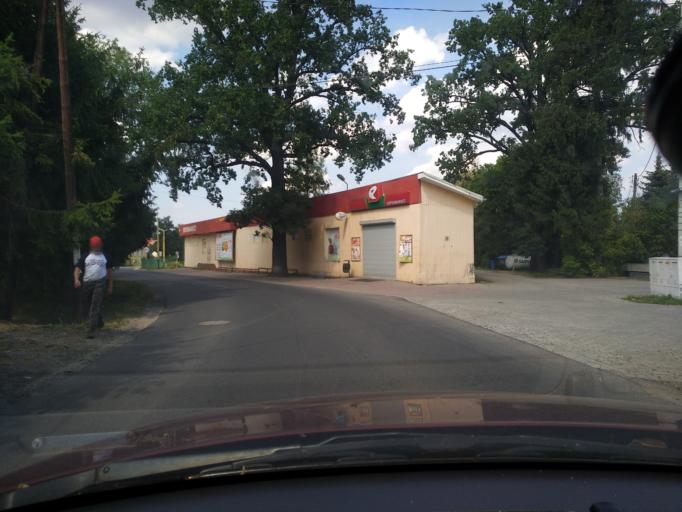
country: PL
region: Lower Silesian Voivodeship
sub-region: Powiat jeleniogorski
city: Stara Kamienica
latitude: 50.9144
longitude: 15.5737
